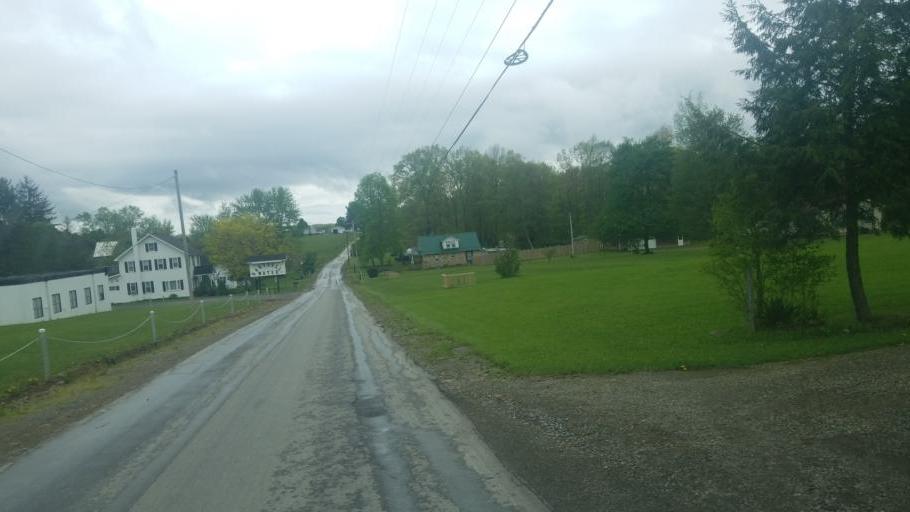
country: US
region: Pennsylvania
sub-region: Forest County
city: Tionesta
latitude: 41.3906
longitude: -79.3881
